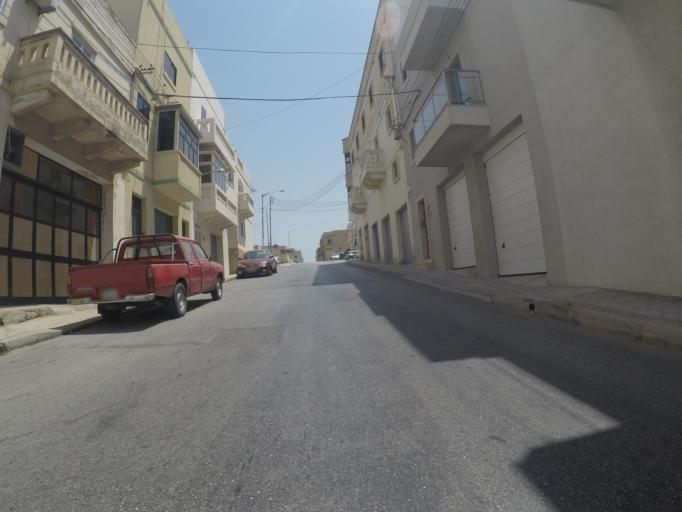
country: MT
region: Ir-Rabat
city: Rabat
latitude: 35.8774
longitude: 14.3959
